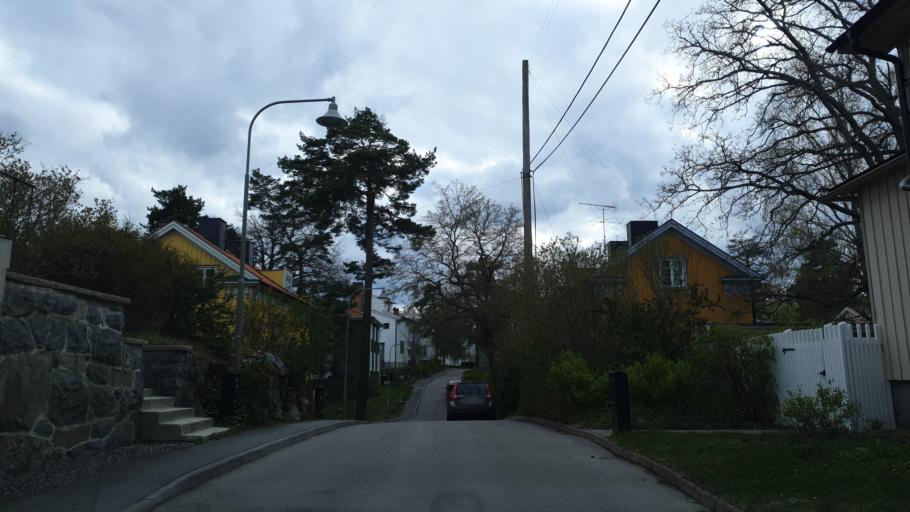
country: SE
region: Stockholm
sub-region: Sundbybergs Kommun
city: Sundbyberg
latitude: 59.3321
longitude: 17.9704
